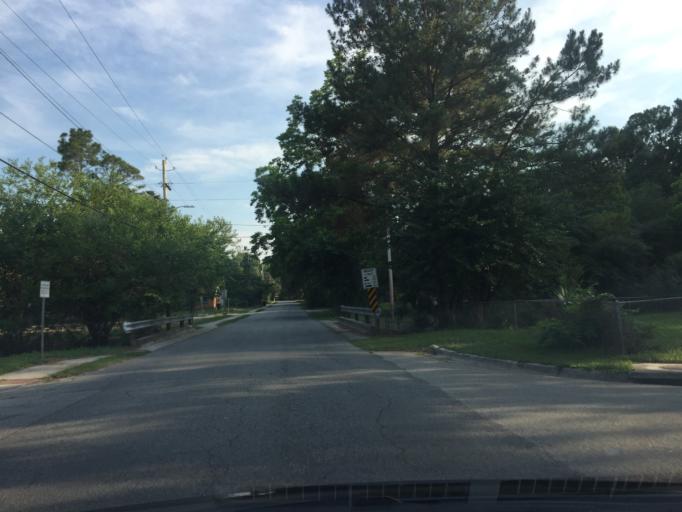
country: US
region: Georgia
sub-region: Chatham County
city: Montgomery
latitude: 31.9956
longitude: -81.1197
